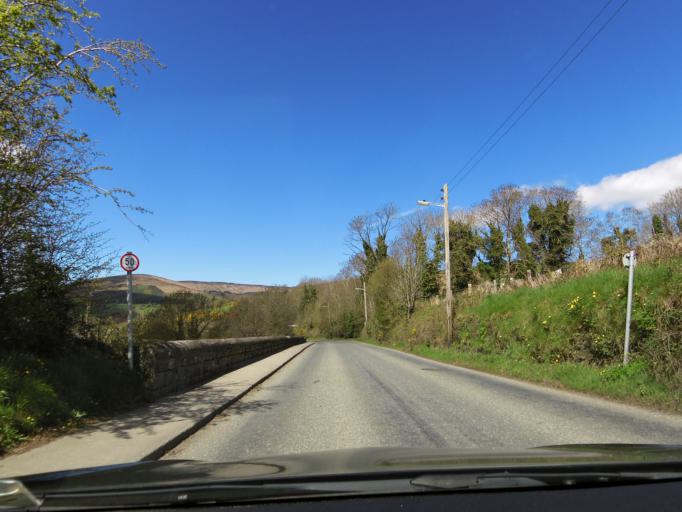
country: IE
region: Leinster
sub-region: Wicklow
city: Carnew
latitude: 52.7965
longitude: -6.4604
